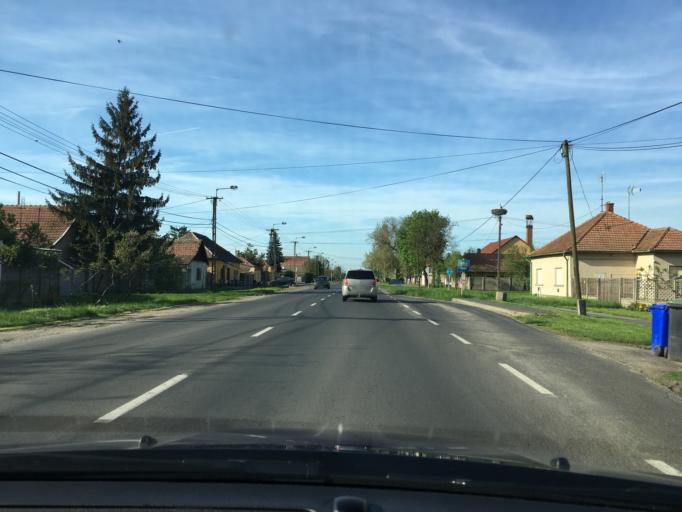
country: HU
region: Bekes
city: Mezobereny
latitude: 46.8373
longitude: 21.0276
